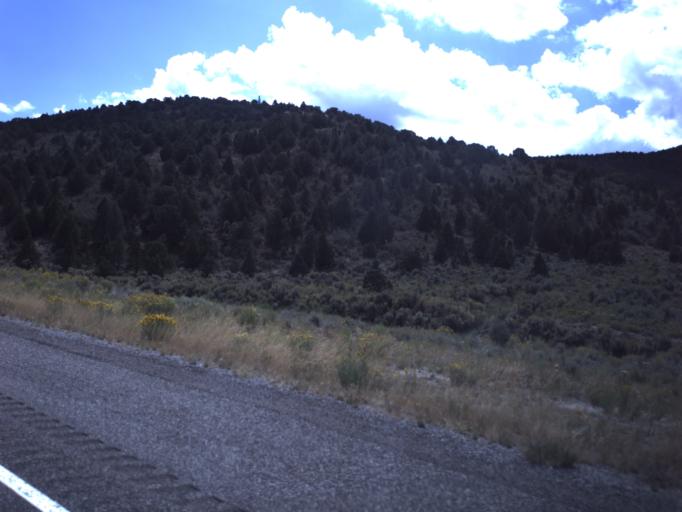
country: US
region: Utah
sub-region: Sevier County
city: Salina
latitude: 38.8053
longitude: -111.5288
